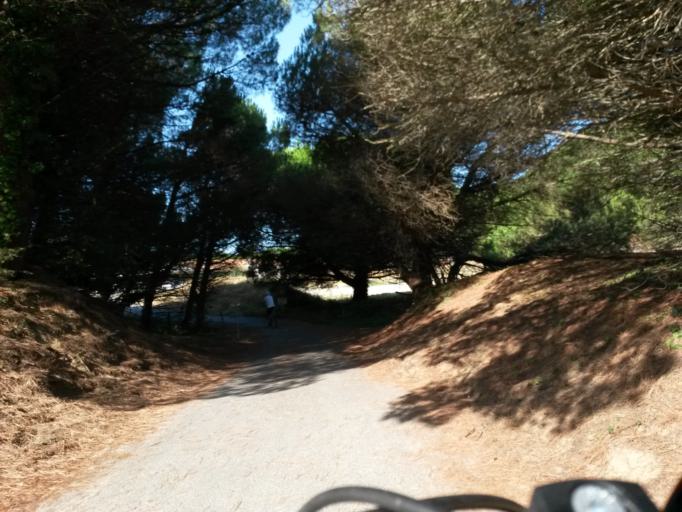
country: FR
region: Poitou-Charentes
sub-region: Departement de la Charente-Maritime
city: Le Bois-Plage-en-Re
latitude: 46.1794
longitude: -1.3745
